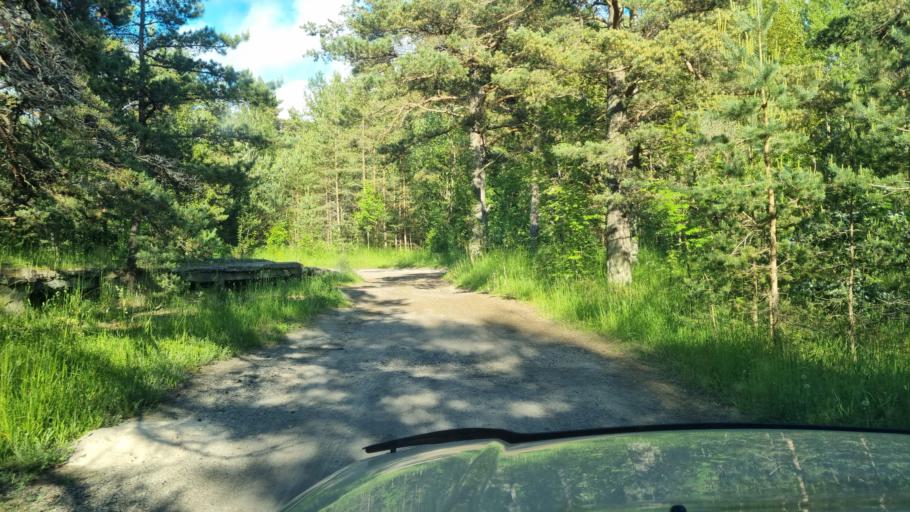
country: LV
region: Ventspils
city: Ventspils
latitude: 57.3635
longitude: 21.5115
